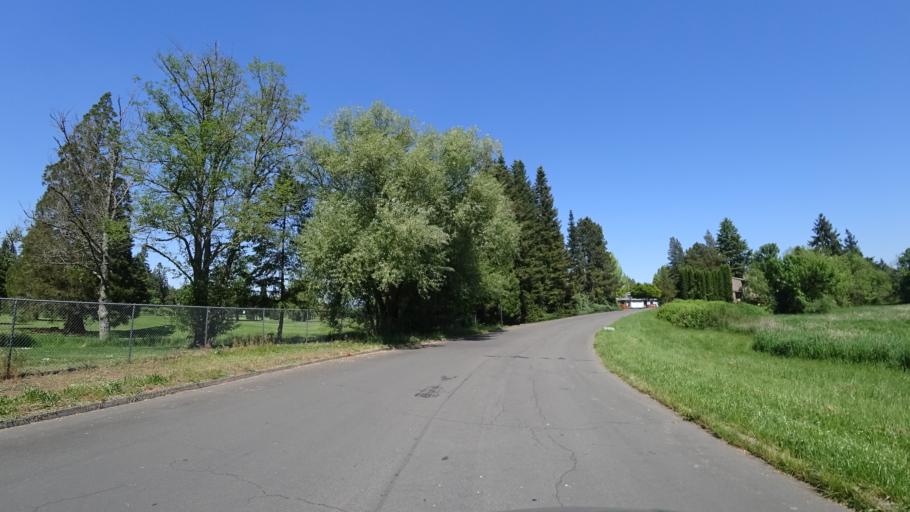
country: US
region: Oregon
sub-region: Washington County
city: Rockcreek
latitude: 45.5490
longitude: -122.8816
